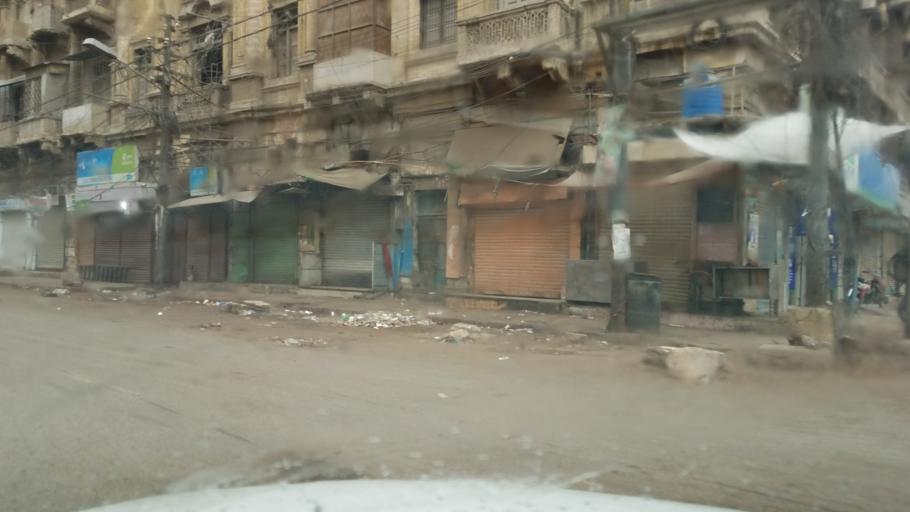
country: PK
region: Sindh
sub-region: Karachi District
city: Karachi
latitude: 24.8500
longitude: 66.9993
